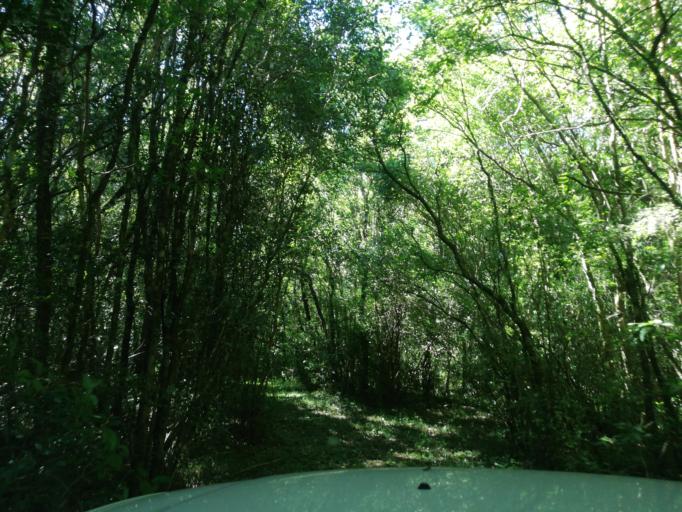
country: AR
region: Misiones
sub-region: Departamento de Leandro N. Alem
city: Leandro N. Alem
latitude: -27.5768
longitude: -55.3728
